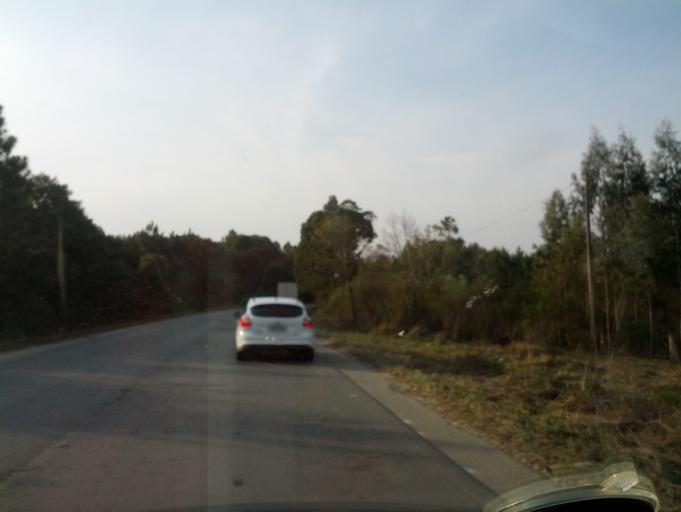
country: BR
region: Santa Catarina
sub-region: Otacilio Costa
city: Otacilio Costa
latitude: -27.5498
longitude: -50.1475
